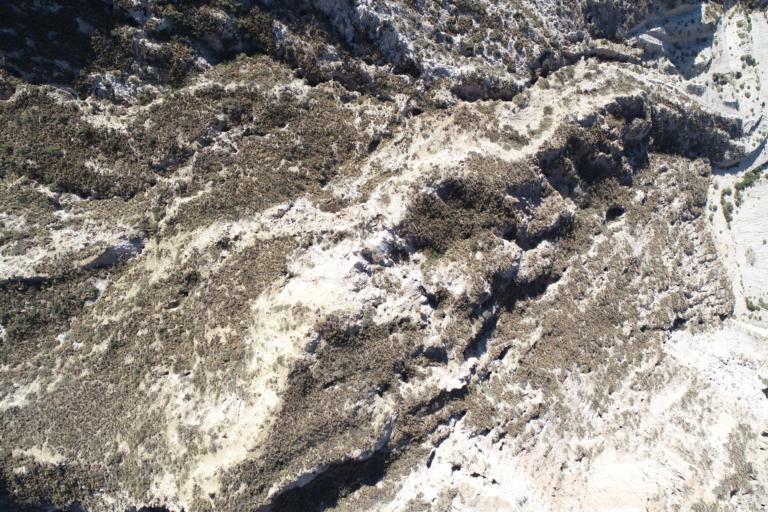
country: BO
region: La Paz
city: La Paz
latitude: -16.5523
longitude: -68.1086
